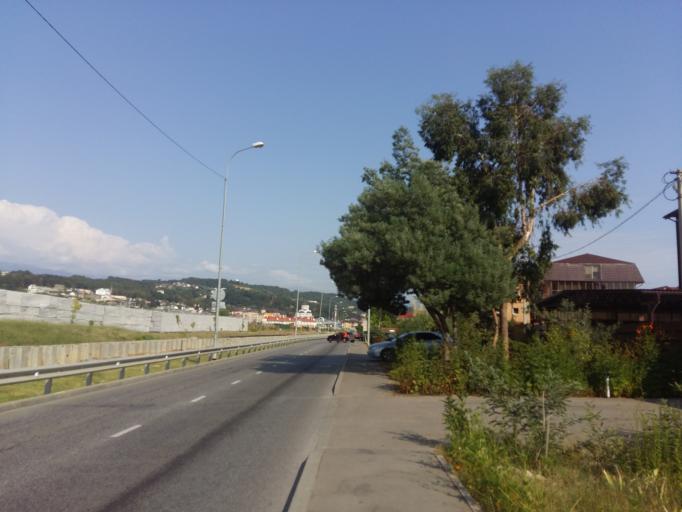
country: RU
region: Krasnodarskiy
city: Adler
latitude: 43.4151
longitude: 39.9591
